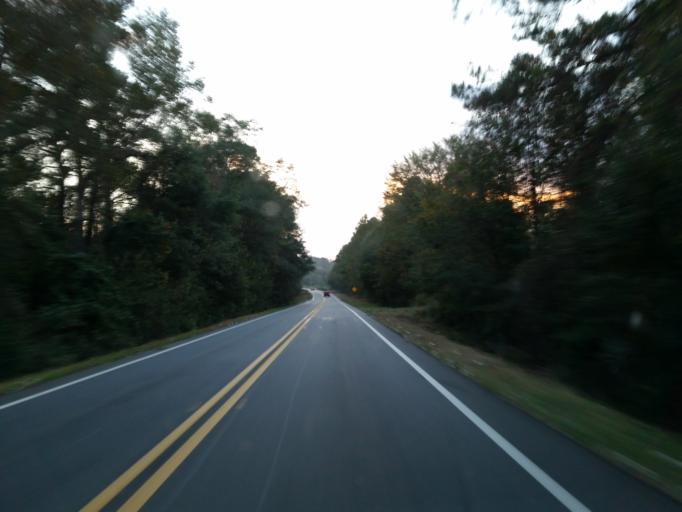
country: US
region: Georgia
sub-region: Pulaski County
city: Hawkinsville
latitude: 32.2215
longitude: -83.5236
